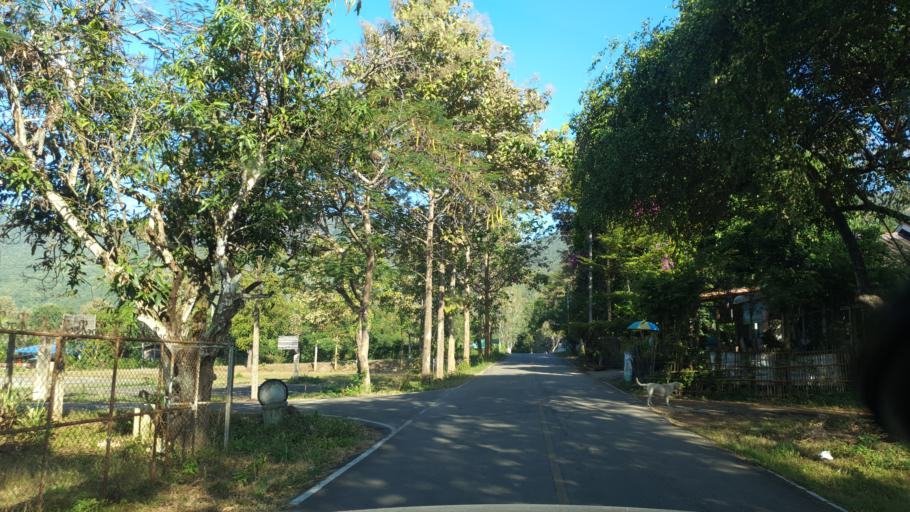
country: TH
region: Chiang Mai
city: Mae On
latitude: 18.7474
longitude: 99.2206
